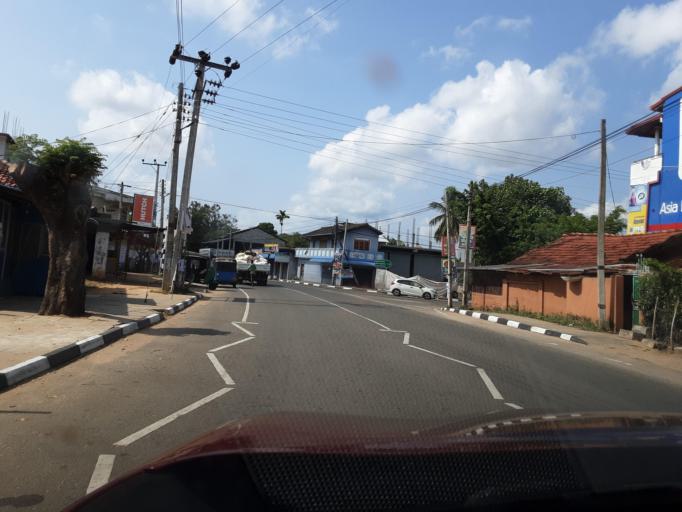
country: LK
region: Southern
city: Tangalla
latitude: 6.2973
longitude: 81.2367
